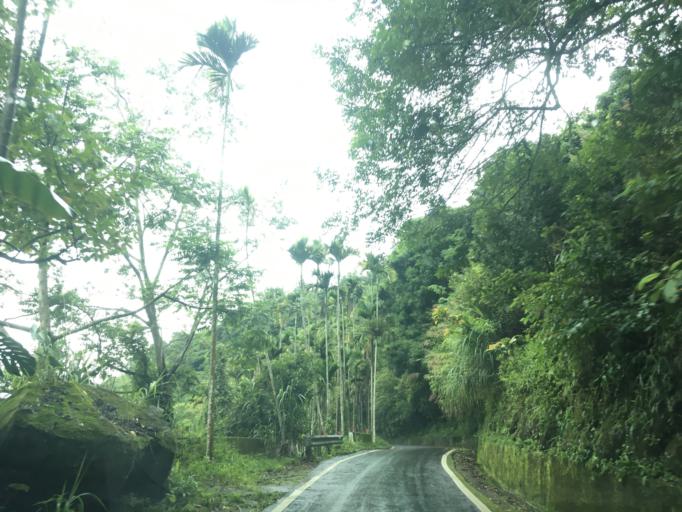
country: TW
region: Taiwan
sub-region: Yunlin
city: Douliu
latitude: 23.5584
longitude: 120.6556
